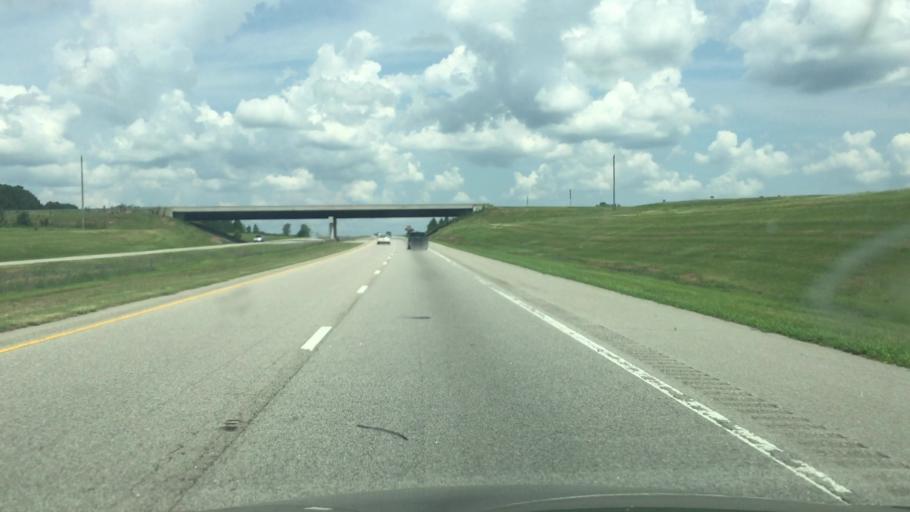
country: US
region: North Carolina
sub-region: Richmond County
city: Ellerbe
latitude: 35.1450
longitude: -79.7138
